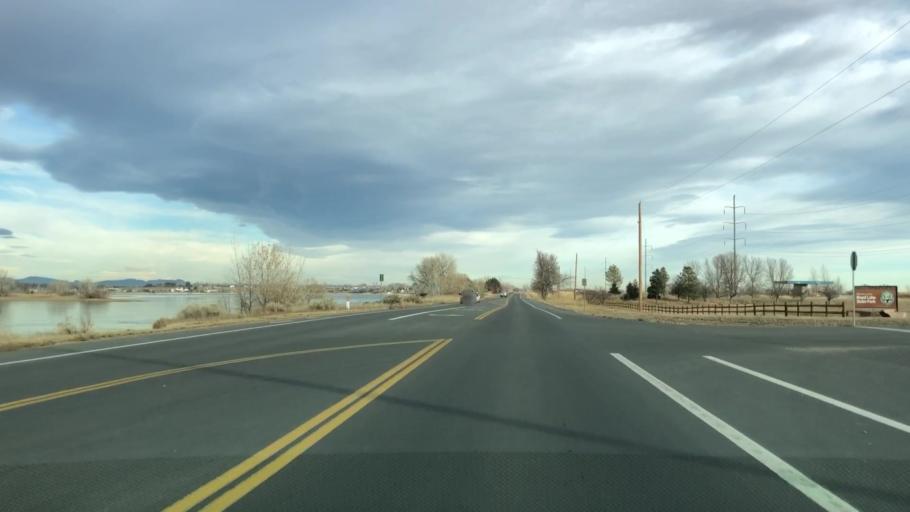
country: US
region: Colorado
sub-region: Larimer County
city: Loveland
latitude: 40.4313
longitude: -105.0454
